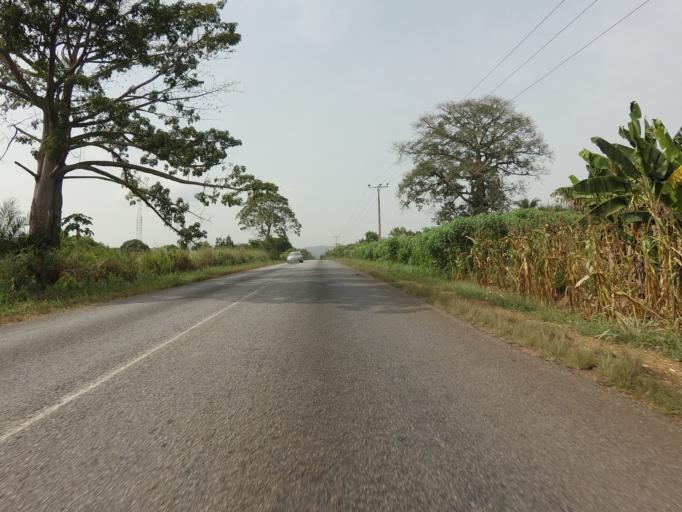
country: GH
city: Akropong
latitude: 6.3065
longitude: 0.1455
